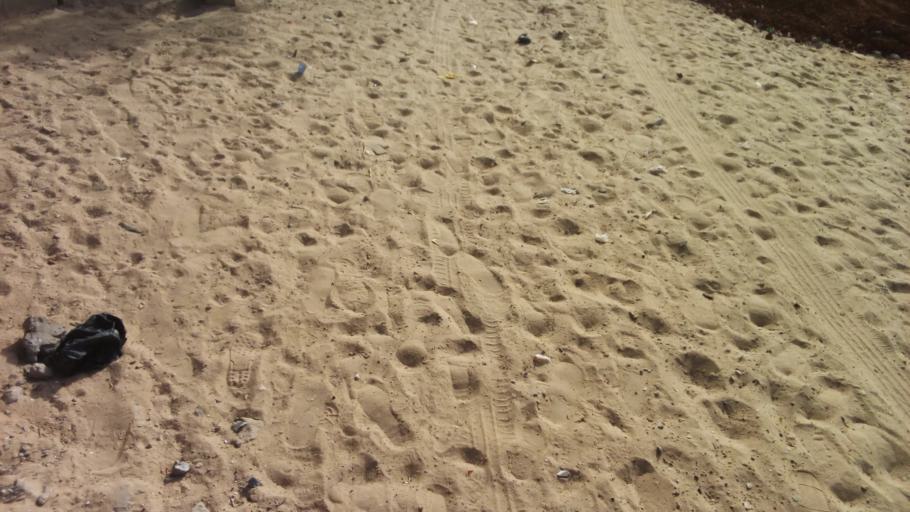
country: SN
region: Dakar
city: Pikine
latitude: 14.8009
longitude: -17.3388
